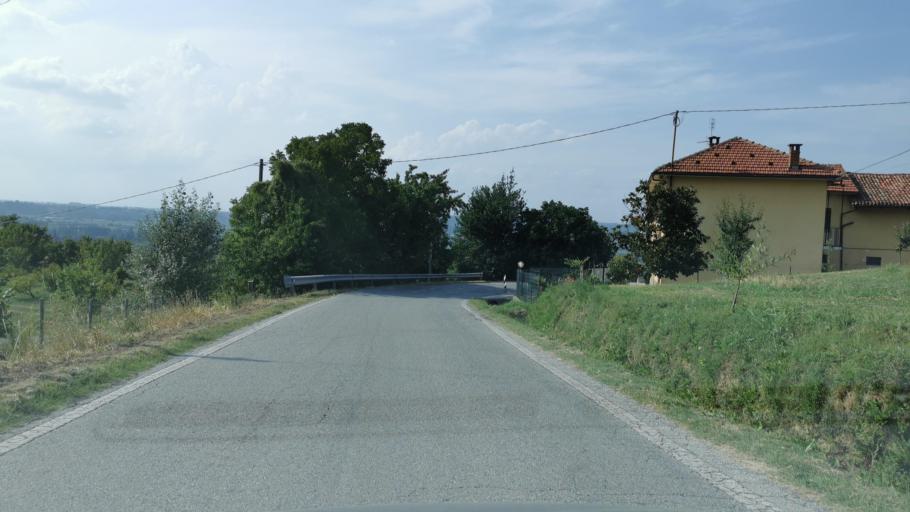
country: IT
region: Piedmont
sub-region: Provincia di Cuneo
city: La Morra
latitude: 44.6486
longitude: 7.8995
